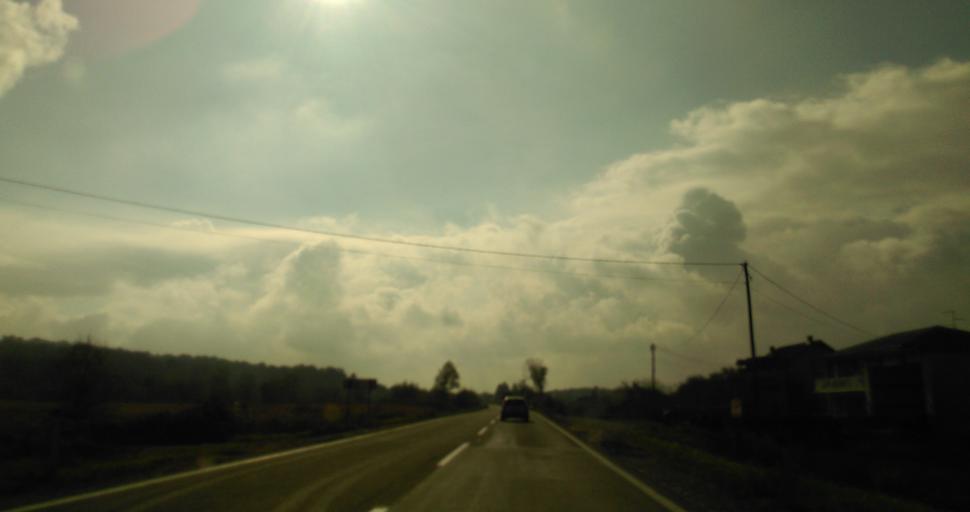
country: RS
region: Central Serbia
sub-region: Belgrade
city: Lazarevac
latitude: 44.3260
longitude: 20.2220
